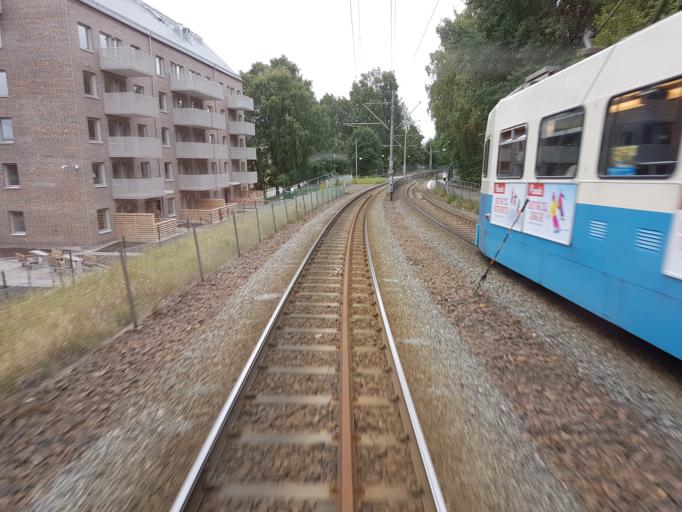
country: SE
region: Vaestra Goetaland
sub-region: Goteborg
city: Majorna
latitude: 57.6632
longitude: 11.9252
